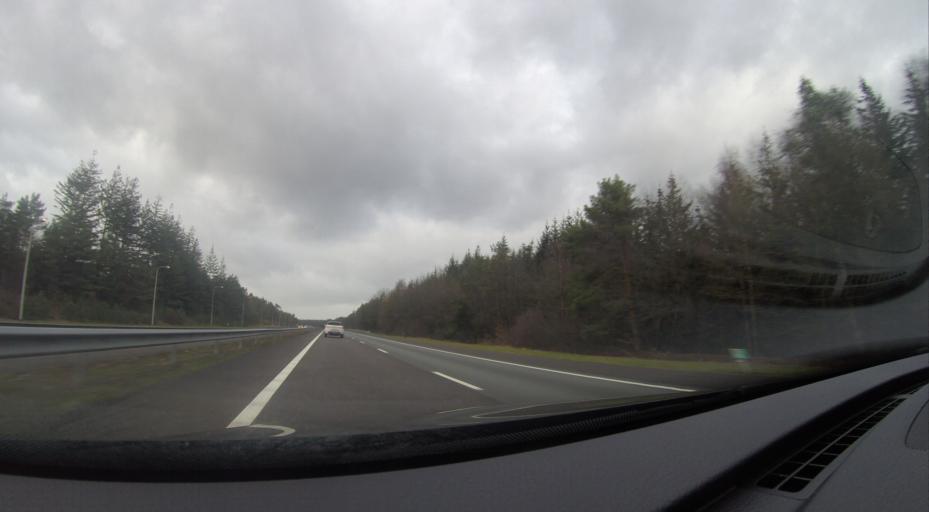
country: NL
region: Gelderland
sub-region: Gemeente Apeldoorn
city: Uddel
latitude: 52.1975
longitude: 5.8330
